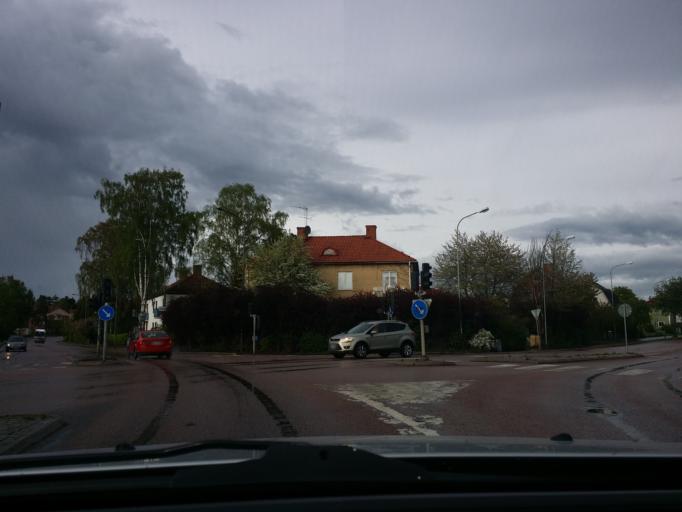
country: SE
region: Vaestmanland
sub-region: Vasteras
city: Vasteras
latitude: 59.6218
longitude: 16.5746
